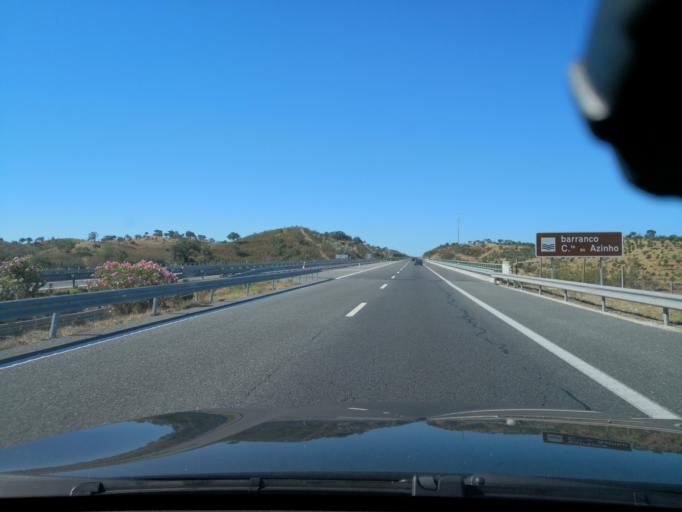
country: PT
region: Beja
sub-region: Almodovar
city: Almodovar
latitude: 37.4858
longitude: -8.2093
